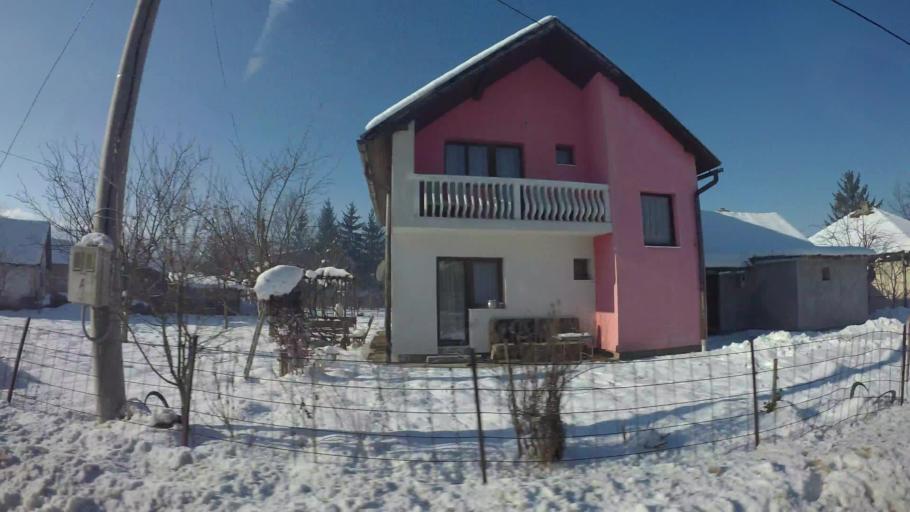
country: BA
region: Federation of Bosnia and Herzegovina
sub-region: Kanton Sarajevo
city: Sarajevo
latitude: 43.8195
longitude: 18.3817
